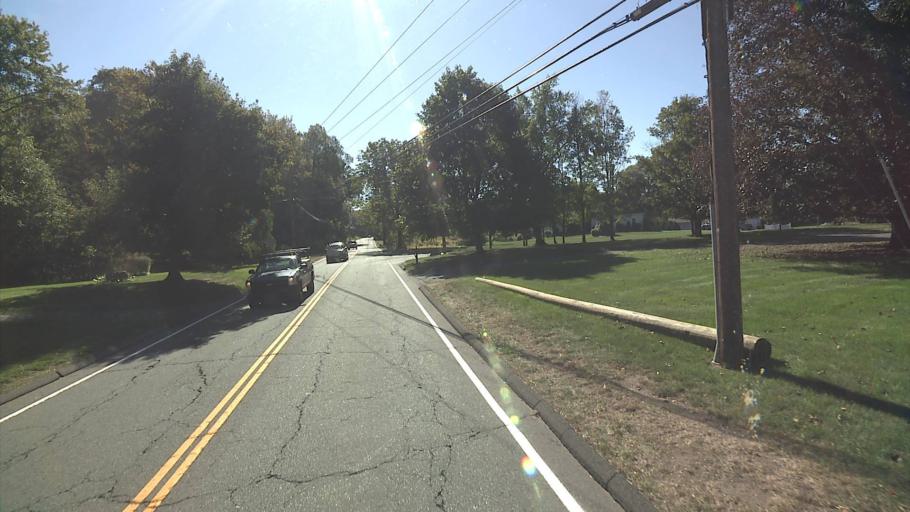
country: US
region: Connecticut
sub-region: Tolland County
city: Somers
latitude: 41.9697
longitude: -72.4429
